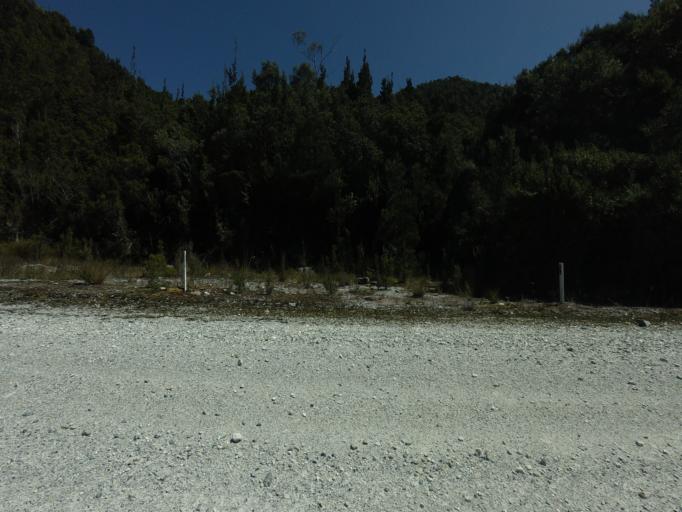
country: AU
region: Tasmania
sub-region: West Coast
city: Queenstown
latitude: -42.7712
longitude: 145.9842
